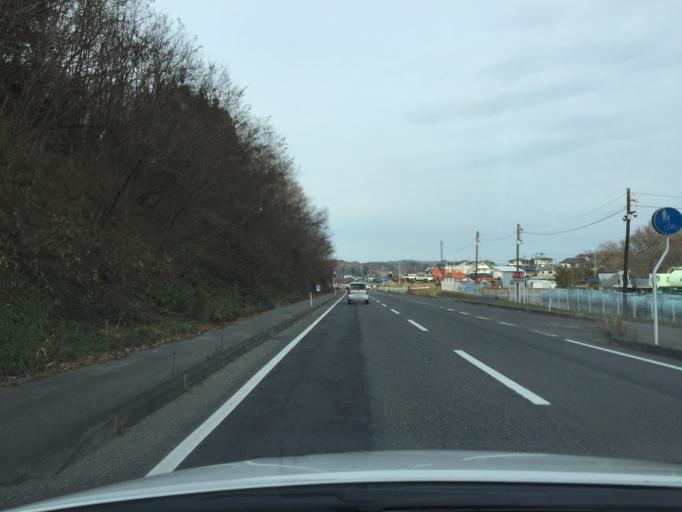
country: JP
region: Fukushima
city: Funehikimachi-funehiki
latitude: 37.4520
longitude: 140.5787
